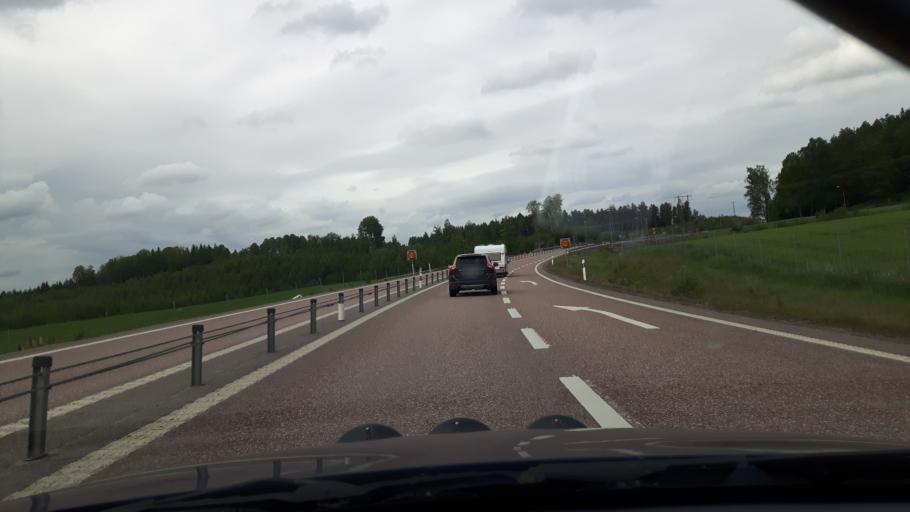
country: SE
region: Soedermanland
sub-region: Flens Kommun
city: Malmkoping
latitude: 59.1443
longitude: 16.7118
